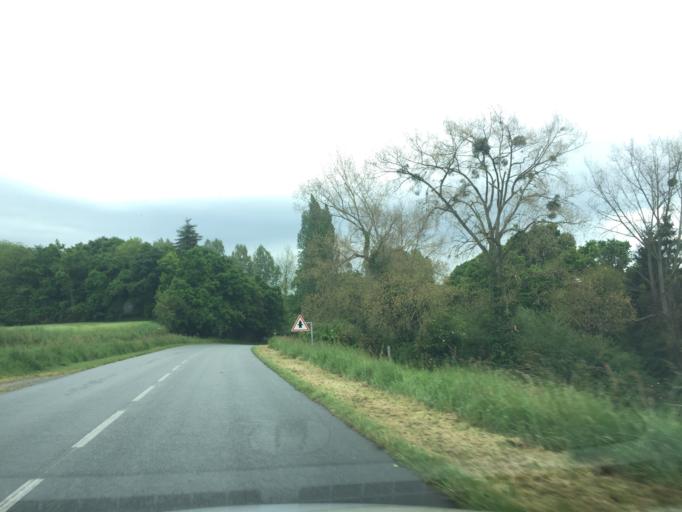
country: FR
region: Brittany
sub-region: Departement des Cotes-d'Armor
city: Crehen
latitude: 48.5416
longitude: -2.2279
